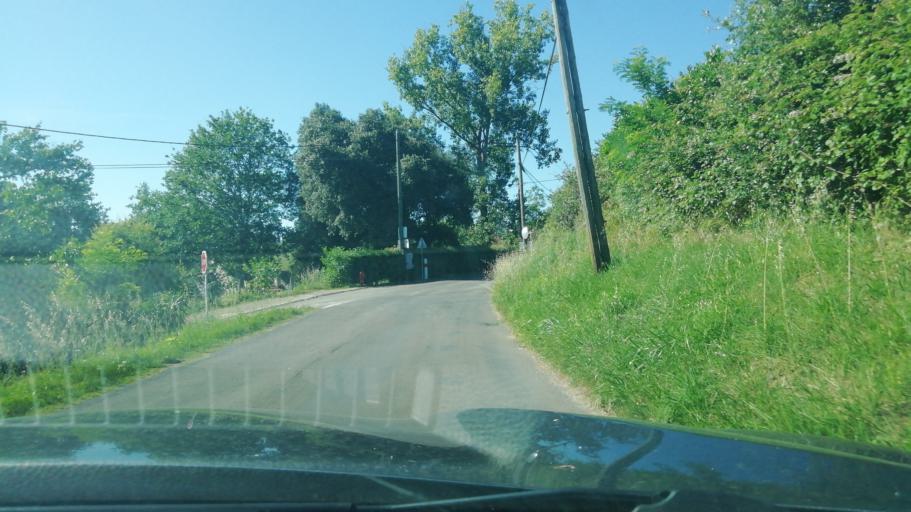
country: FR
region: Aquitaine
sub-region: Departement de la Dordogne
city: Sarlat-la-Caneda
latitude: 44.8646
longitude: 1.2227
